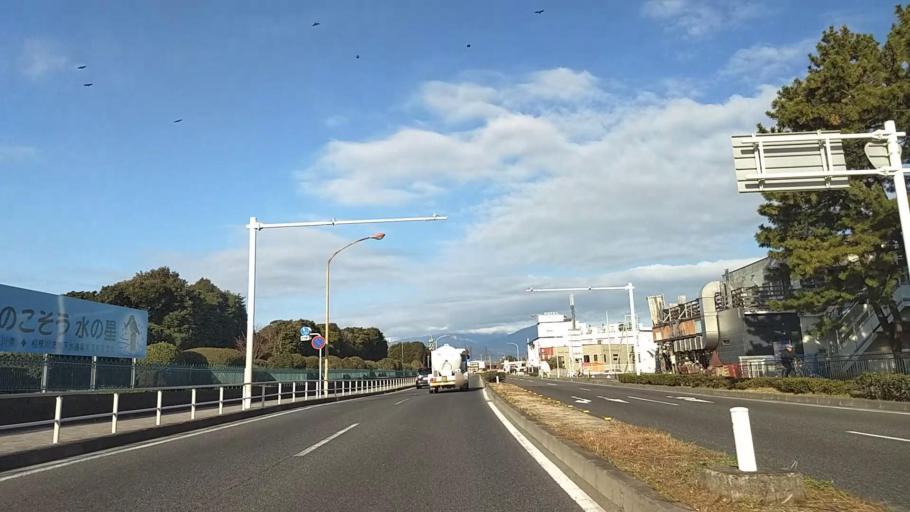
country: JP
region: Kanagawa
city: Chigasaki
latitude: 35.3179
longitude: 139.3810
